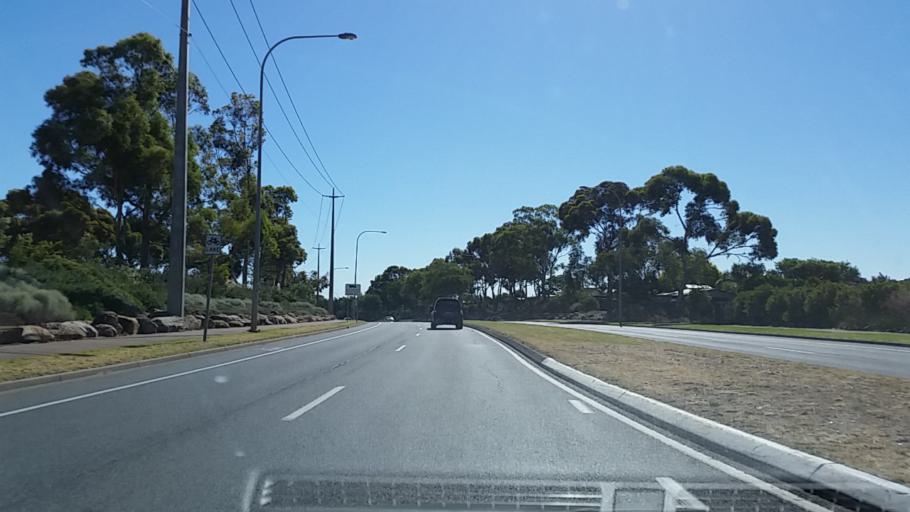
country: AU
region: South Australia
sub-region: Tea Tree Gully
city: Modbury
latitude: -34.8066
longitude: 138.6807
